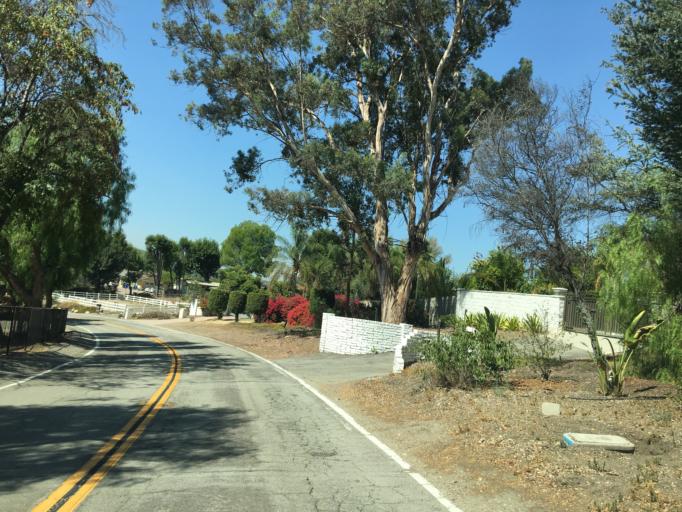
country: US
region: California
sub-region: Los Angeles County
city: Charter Oak
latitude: 34.0705
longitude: -117.8546
